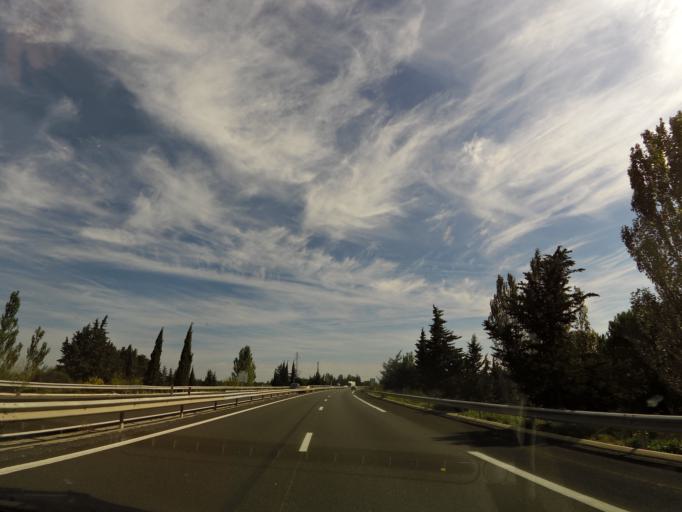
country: FR
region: Languedoc-Roussillon
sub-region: Departement du Gard
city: Caissargues
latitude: 43.8064
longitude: 4.3696
